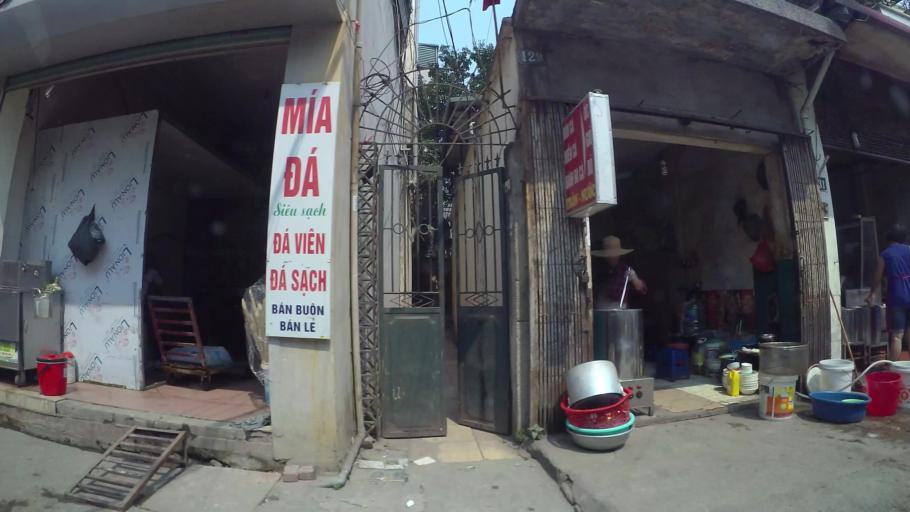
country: VN
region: Ha Noi
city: Thanh Xuan
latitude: 21.0048
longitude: 105.8114
